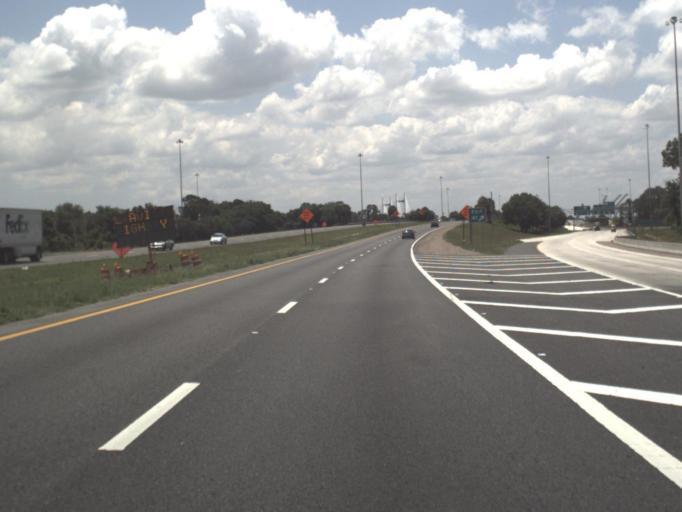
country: US
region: Florida
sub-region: Duval County
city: Jacksonville
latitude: 30.4169
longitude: -81.5655
